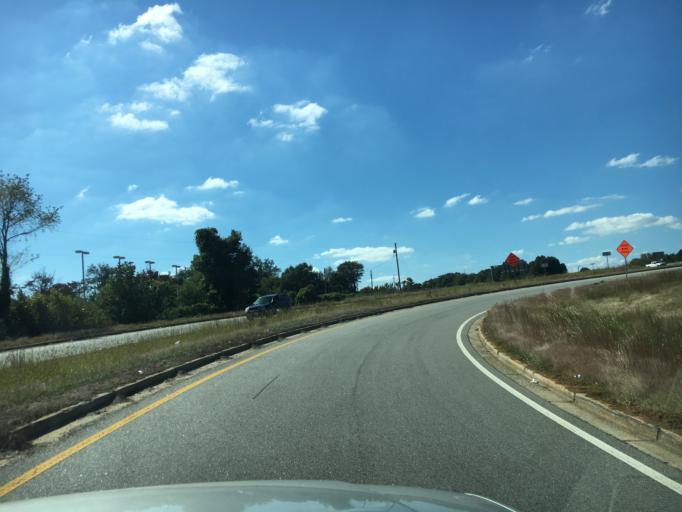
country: US
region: South Carolina
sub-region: Greenville County
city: Mauldin
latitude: 34.8126
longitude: -82.3368
